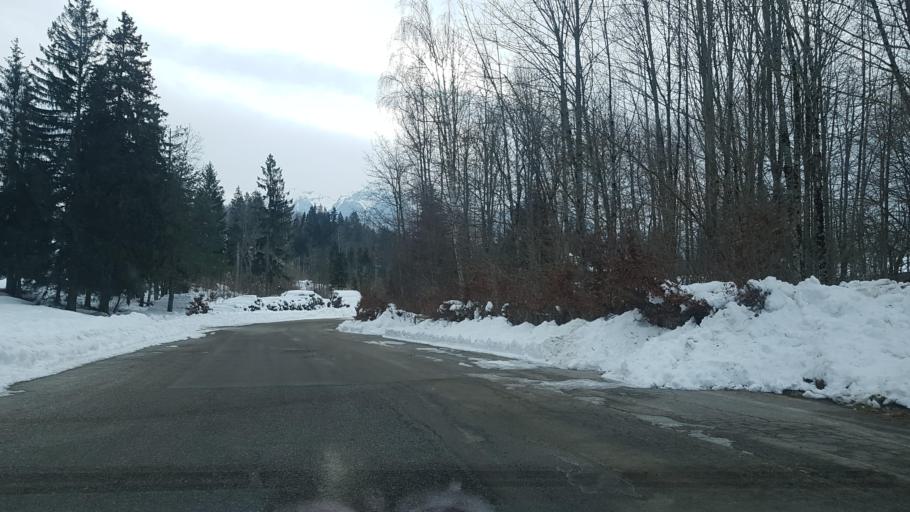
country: IT
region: Friuli Venezia Giulia
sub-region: Provincia di Udine
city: Lauco
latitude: 46.4288
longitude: 12.9461
